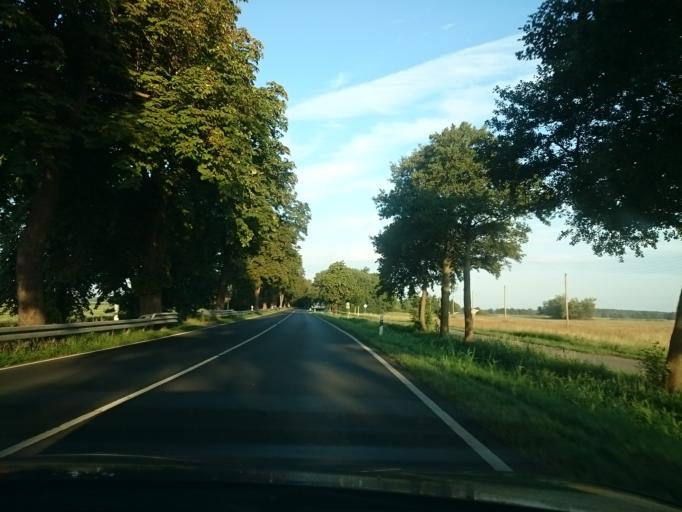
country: DE
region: Mecklenburg-Vorpommern
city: Ostseebad Zinnowitz
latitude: 54.0684
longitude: 13.8940
